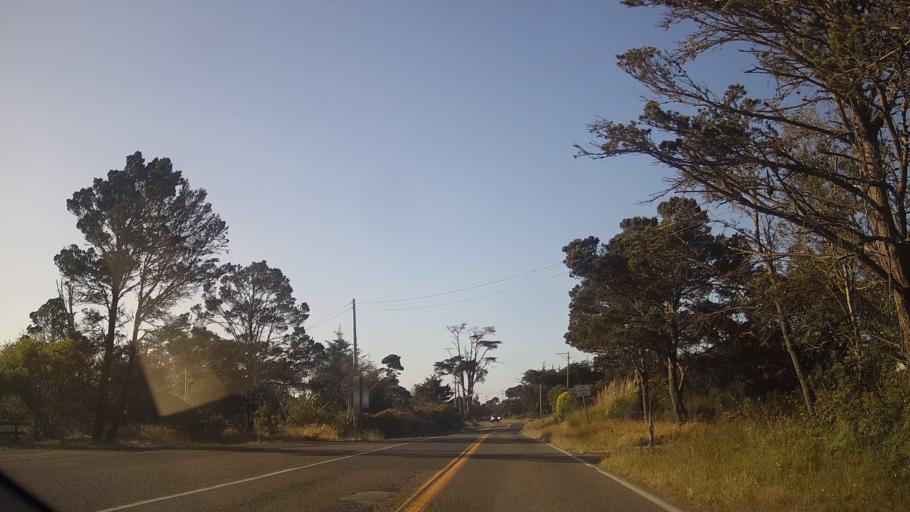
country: US
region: California
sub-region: Mendocino County
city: Fort Bragg
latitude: 39.4738
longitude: -123.7978
